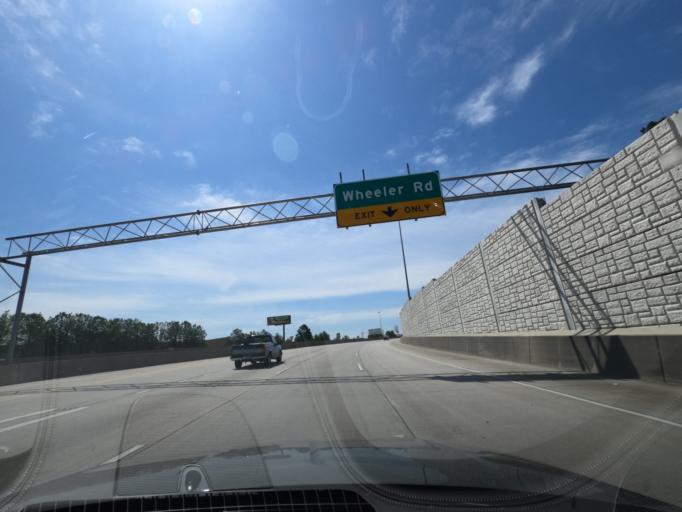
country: US
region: Georgia
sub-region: Columbia County
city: Martinez
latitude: 33.4887
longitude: -82.0831
